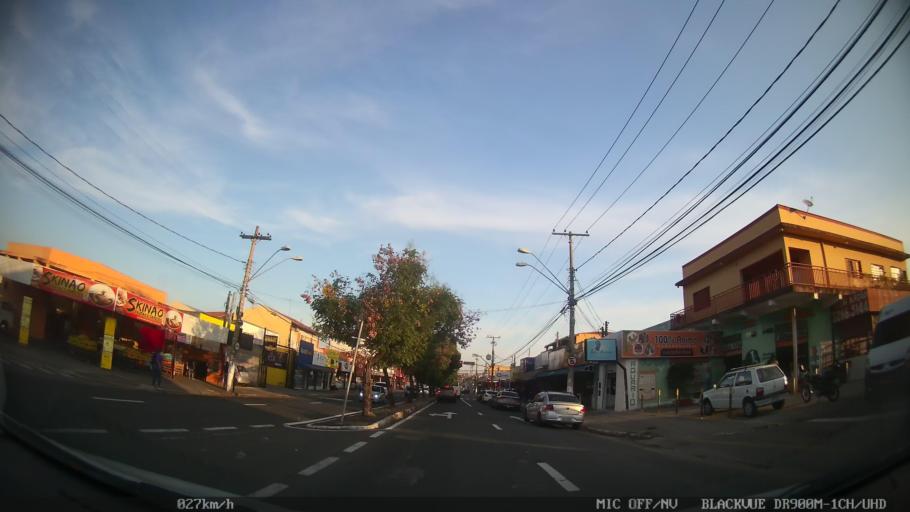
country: BR
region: Sao Paulo
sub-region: Campinas
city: Campinas
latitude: -22.9704
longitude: -47.1283
